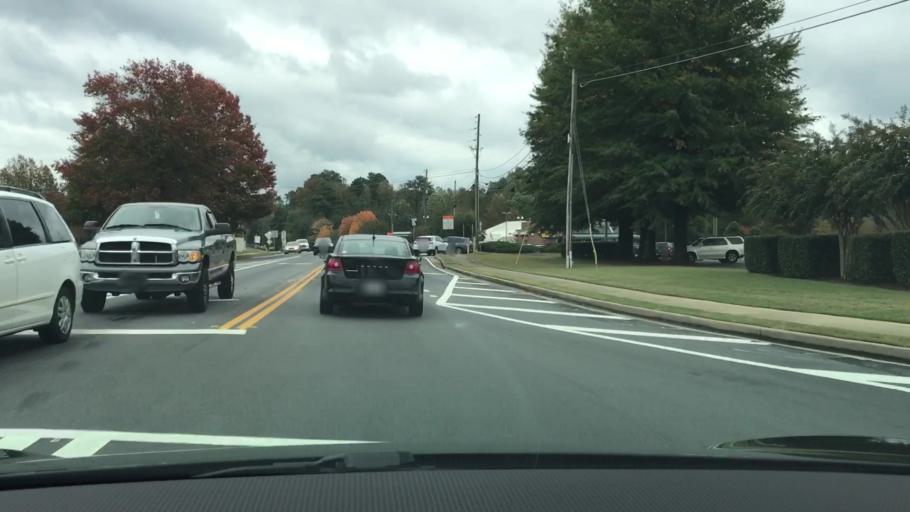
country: US
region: Georgia
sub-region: Oconee County
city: Watkinsville
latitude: 33.8732
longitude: -83.4415
